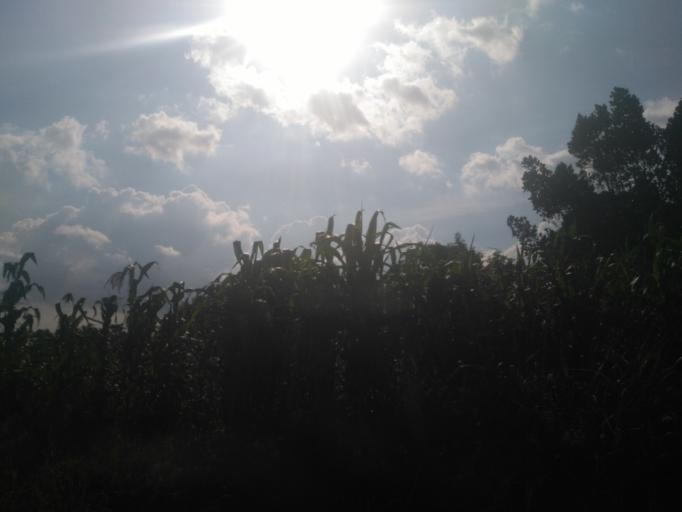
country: UG
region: Central Region
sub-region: Wakiso District
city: Wakiso
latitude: 0.3000
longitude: 32.4475
